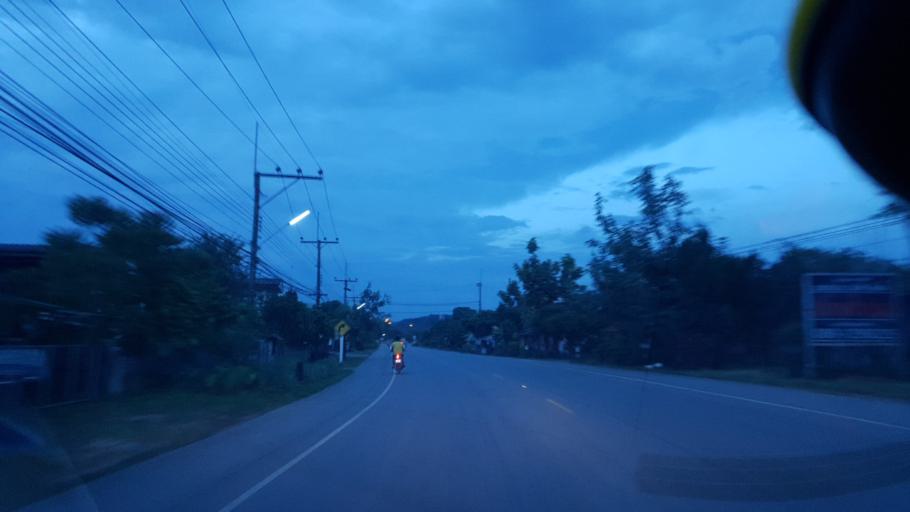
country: TH
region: Chiang Rai
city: Wiang Chiang Rung
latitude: 19.9837
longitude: 100.0258
